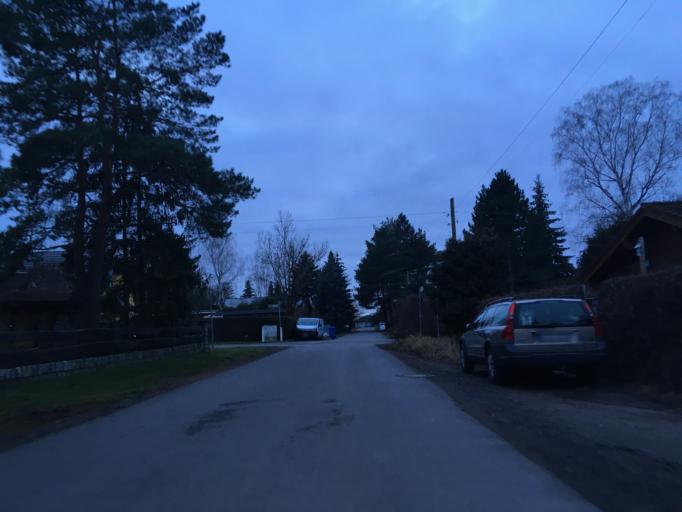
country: DE
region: Berlin
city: Karow
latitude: 52.6061
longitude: 13.4832
